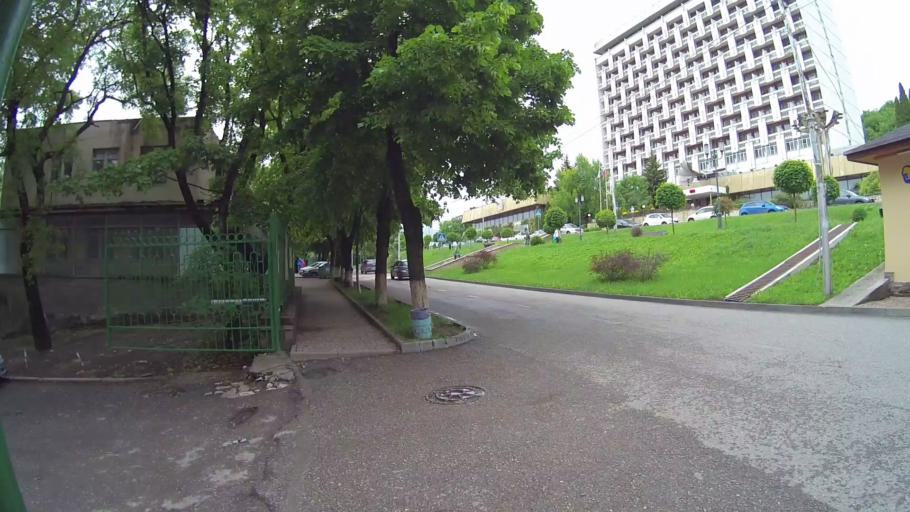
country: RU
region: Stavropol'skiy
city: Goryachevodskiy
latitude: 44.0440
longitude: 43.0977
